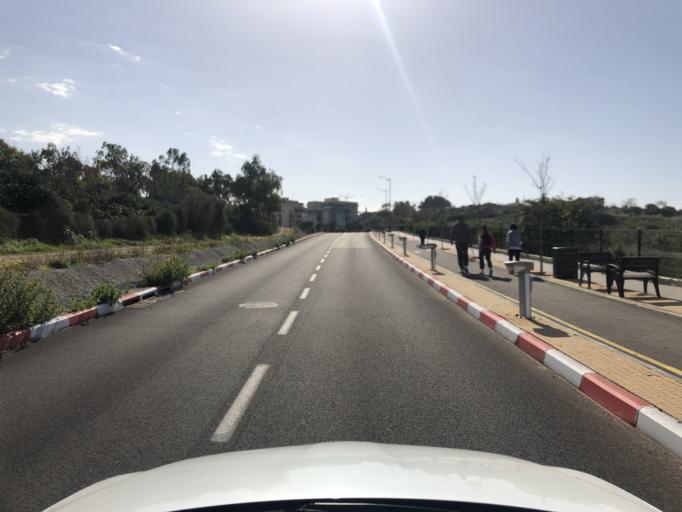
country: IL
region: Central District
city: Ness Ziona
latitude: 31.9184
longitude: 34.7855
